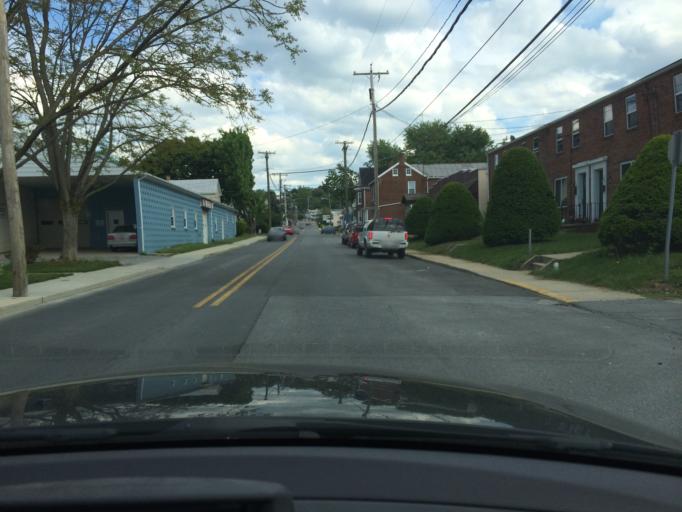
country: US
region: Maryland
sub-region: Carroll County
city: Westminster
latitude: 39.5679
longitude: -76.9906
